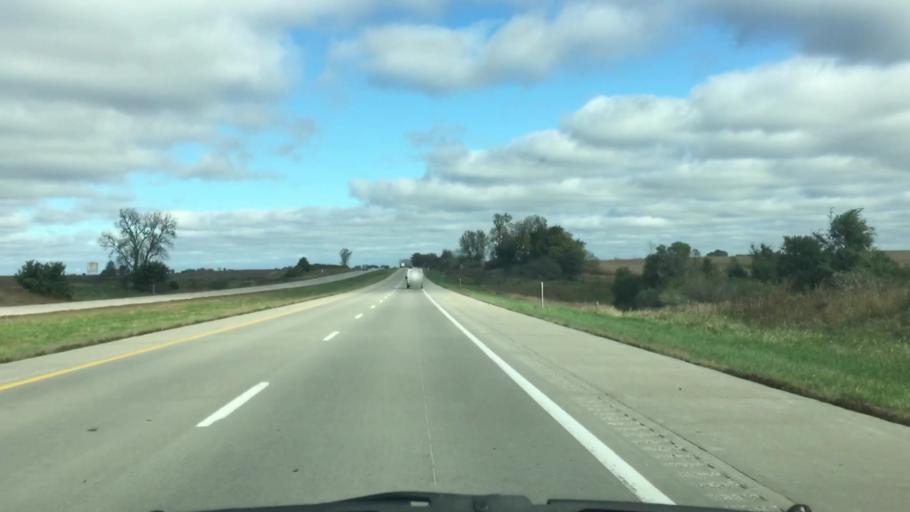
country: US
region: Iowa
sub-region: Clarke County
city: Osceola
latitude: 40.9205
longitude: -93.7969
